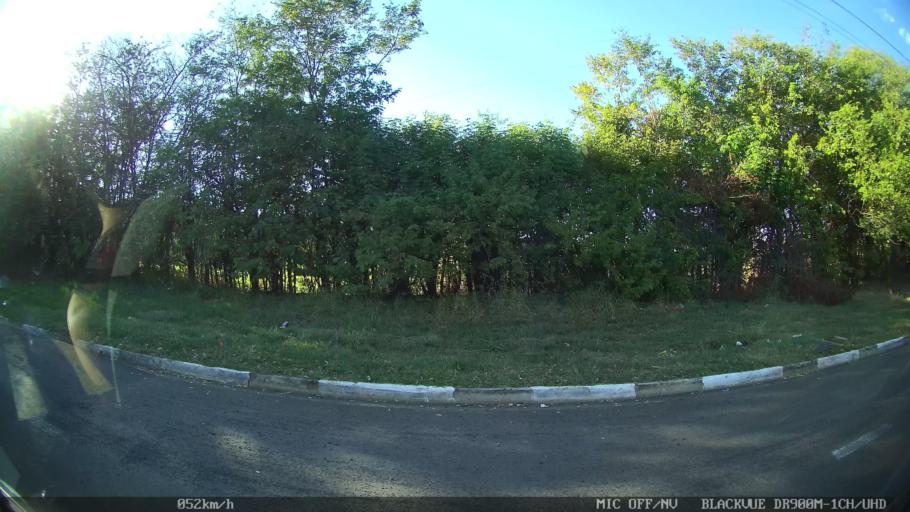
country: BR
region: Sao Paulo
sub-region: Franca
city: Franca
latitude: -20.5695
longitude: -47.3665
